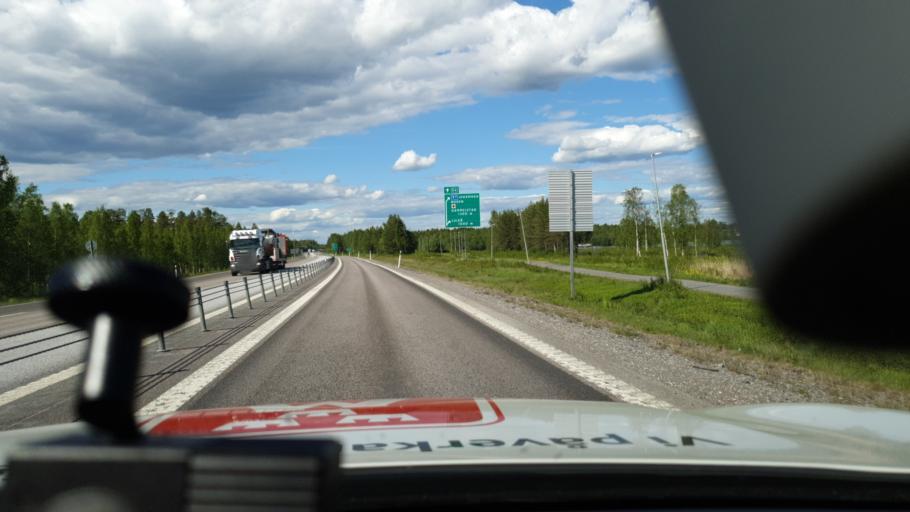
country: SE
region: Norrbotten
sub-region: Lulea Kommun
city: Gammelstad
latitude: 65.6113
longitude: 22.0554
